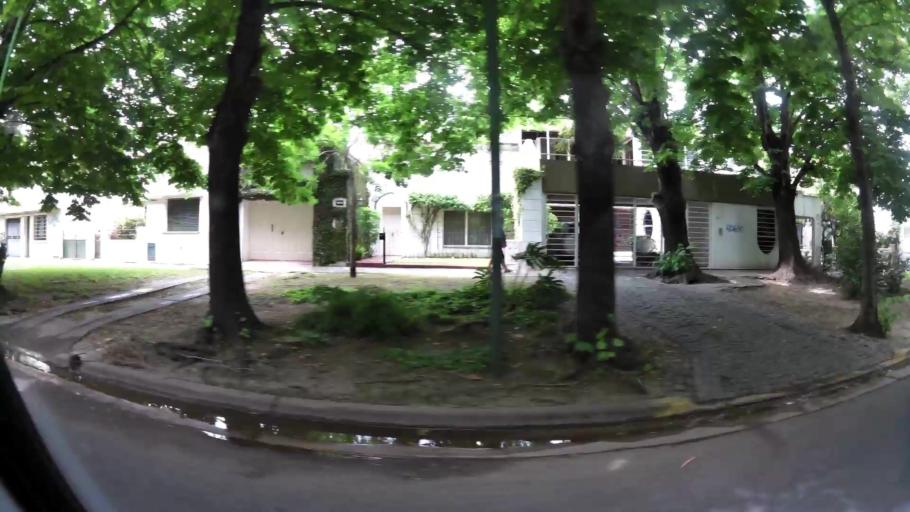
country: AR
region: Buenos Aires
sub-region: Partido de La Plata
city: La Plata
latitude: -34.9354
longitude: -57.9710
